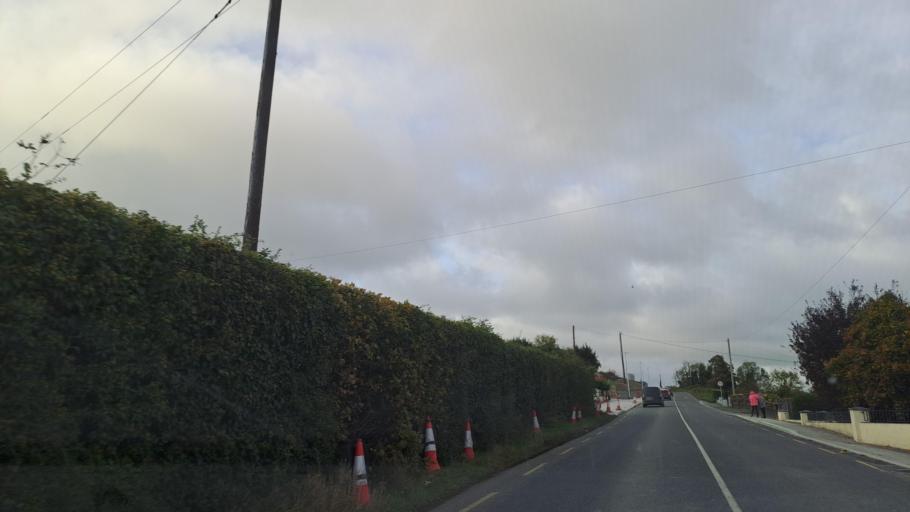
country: IE
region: Ulster
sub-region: An Cabhan
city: Kingscourt
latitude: 53.8958
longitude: -6.8027
